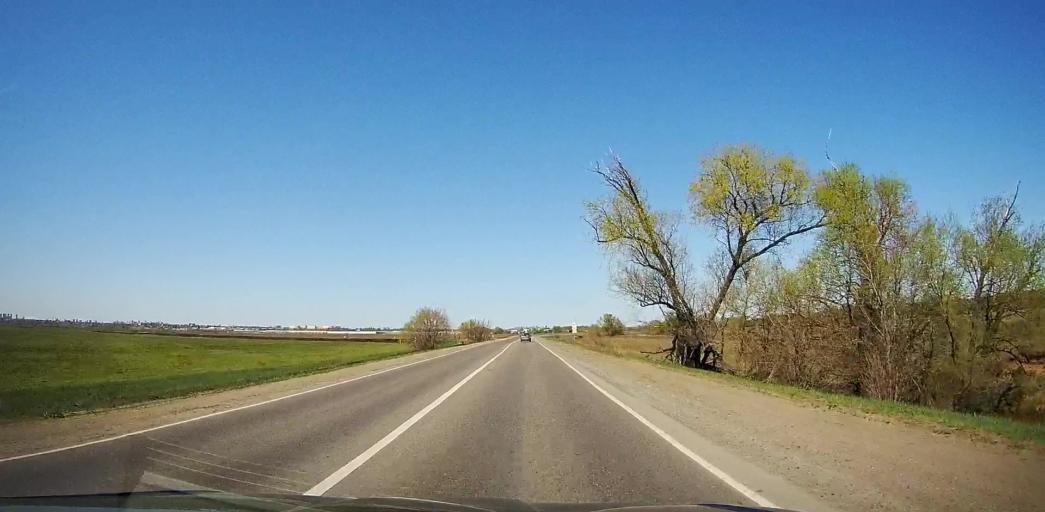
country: RU
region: Moskovskaya
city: Ramenskoye
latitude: 55.5243
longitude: 38.2771
